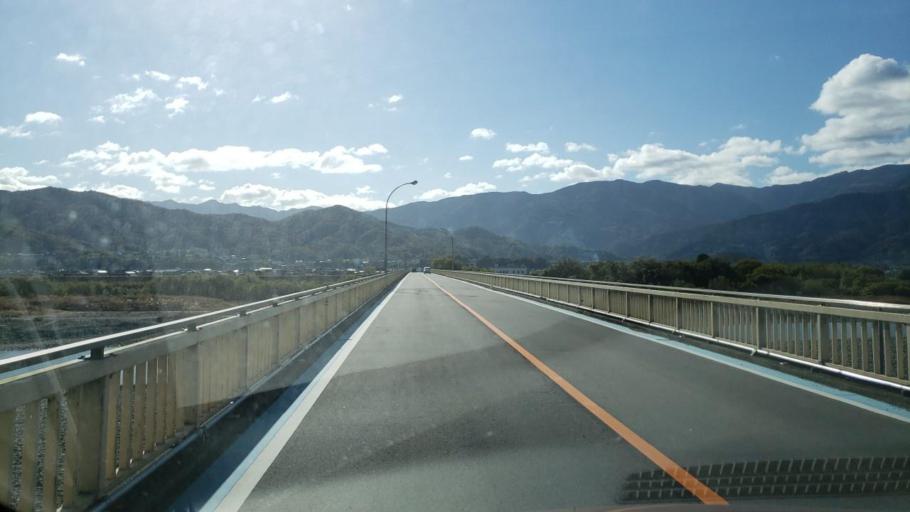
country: JP
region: Tokushima
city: Wakimachi
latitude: 34.0708
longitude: 134.2367
